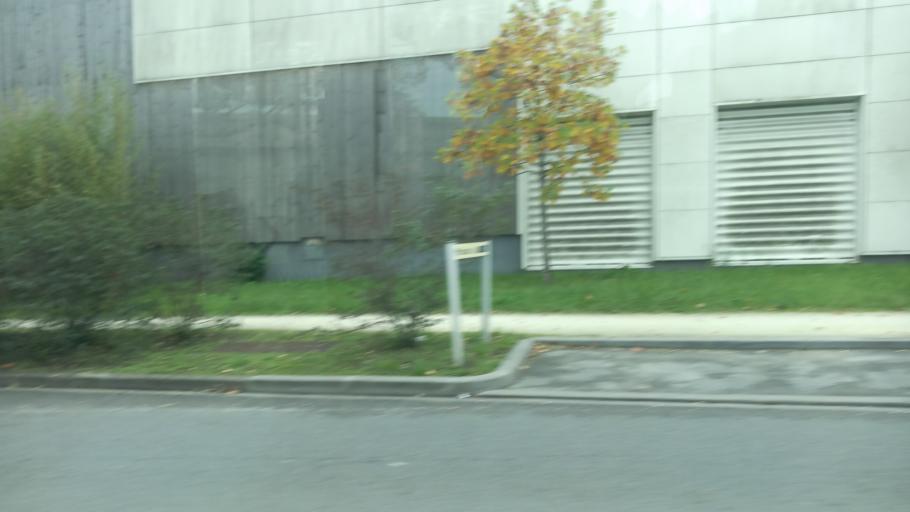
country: FR
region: Aquitaine
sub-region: Departement de la Gironde
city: Begles
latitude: 44.7967
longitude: -0.5303
